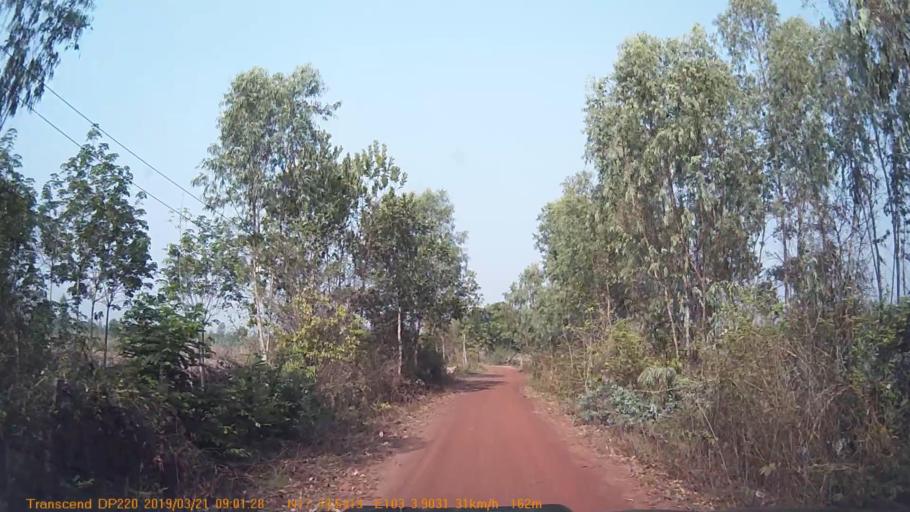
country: TH
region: Changwat Udon Thani
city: Phibun Rak
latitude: 17.6590
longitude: 103.0648
